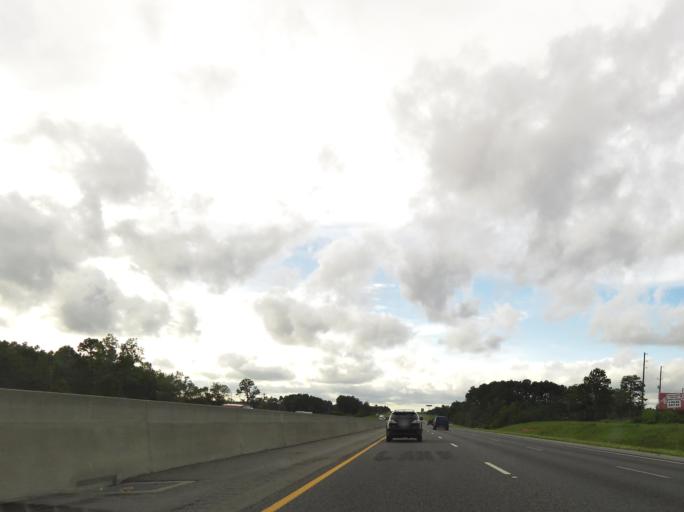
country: US
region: Georgia
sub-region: Turner County
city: Ashburn
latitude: 31.6509
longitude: -83.5959
